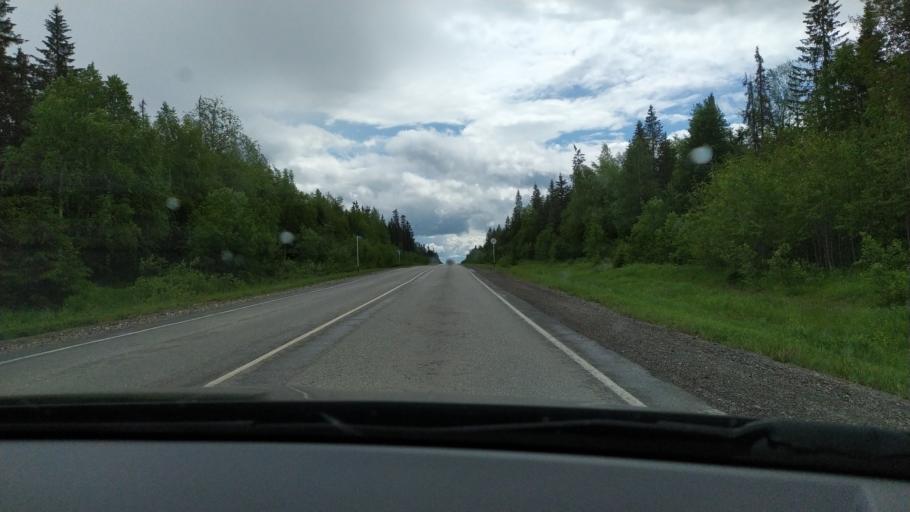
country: RU
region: Perm
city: Gremyachinsk
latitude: 58.5097
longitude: 57.8118
